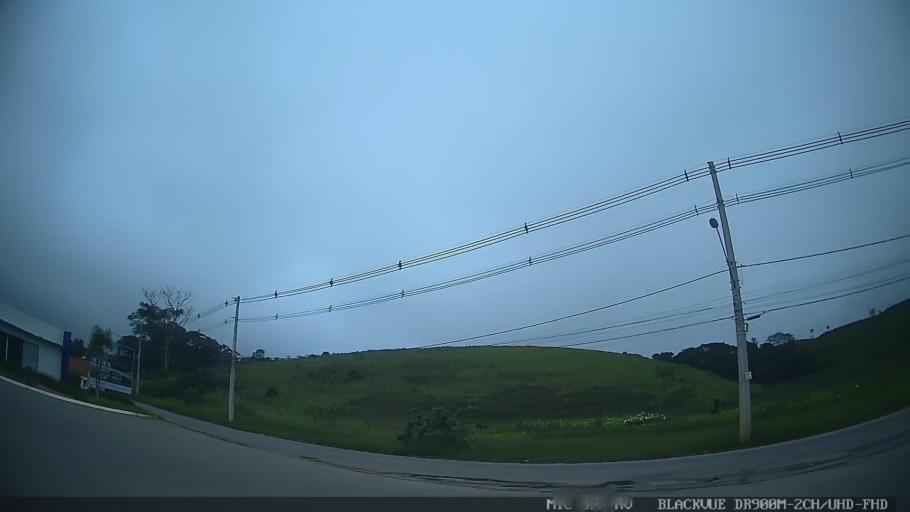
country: BR
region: Sao Paulo
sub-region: Mogi das Cruzes
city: Mogi das Cruzes
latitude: -23.5324
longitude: -46.1407
